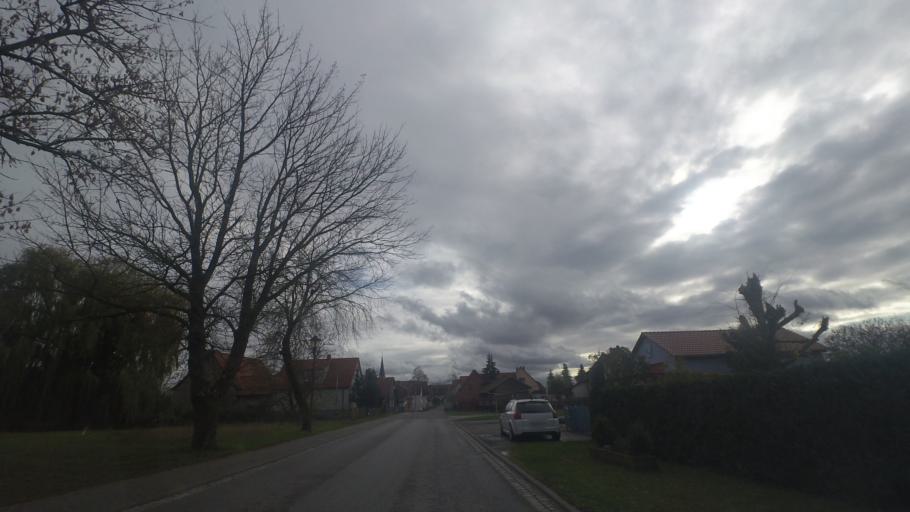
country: DE
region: Bavaria
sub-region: Regierungsbezirk Unterfranken
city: Hochheim
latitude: 50.3846
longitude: 10.4709
